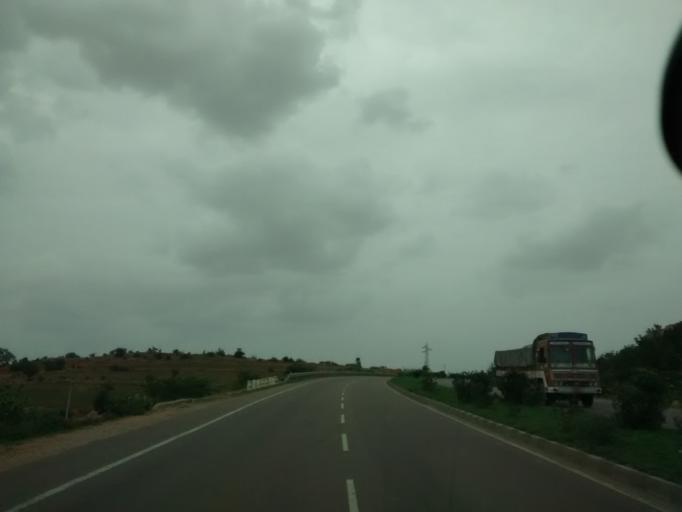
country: IN
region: Andhra Pradesh
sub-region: Kurnool
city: Ramapuram
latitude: 15.1839
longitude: 77.6887
